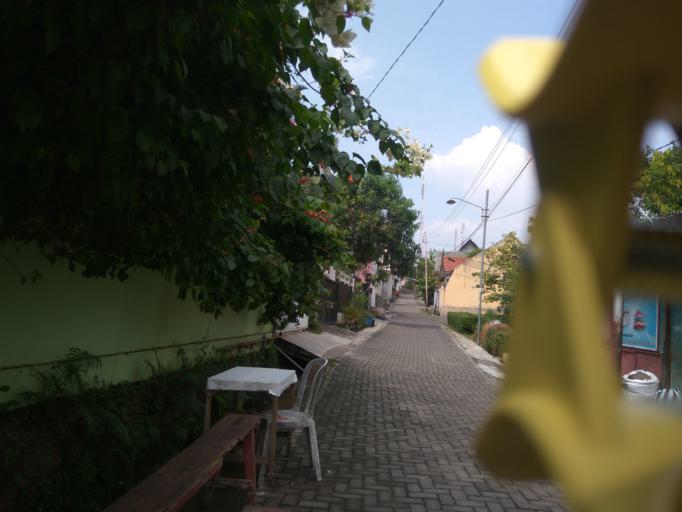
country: ID
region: Central Java
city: Semarang
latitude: -7.0431
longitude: 110.4185
